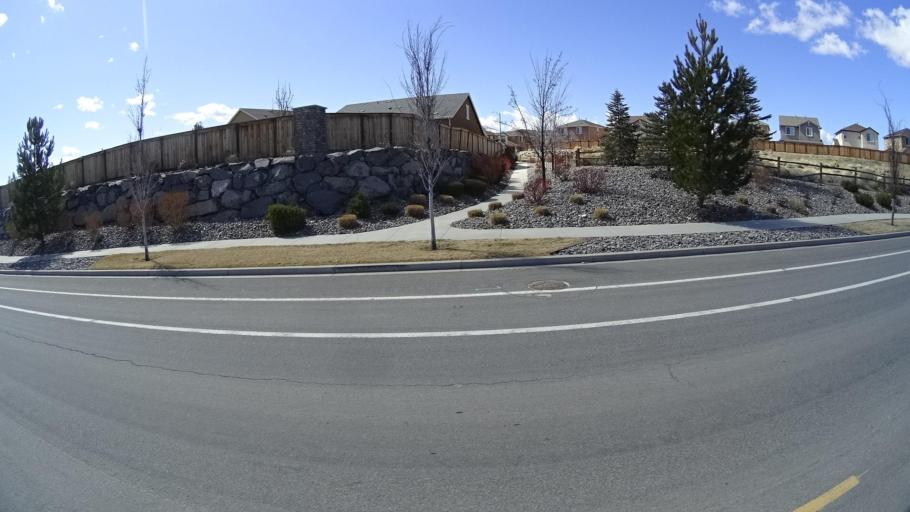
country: US
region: Nevada
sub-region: Washoe County
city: Lemmon Valley
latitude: 39.6479
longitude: -119.8678
